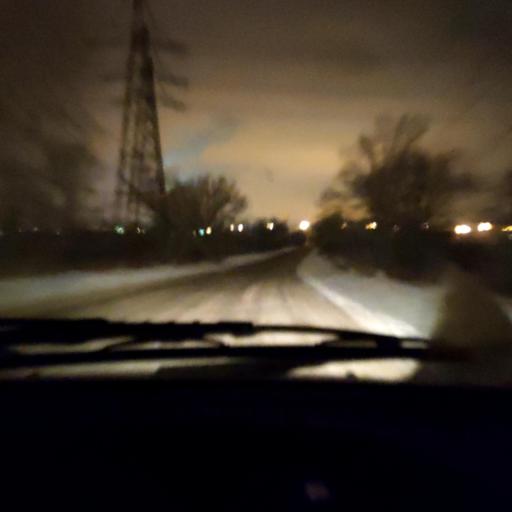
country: RU
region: Samara
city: Zhigulevsk
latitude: 53.4839
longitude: 49.5053
